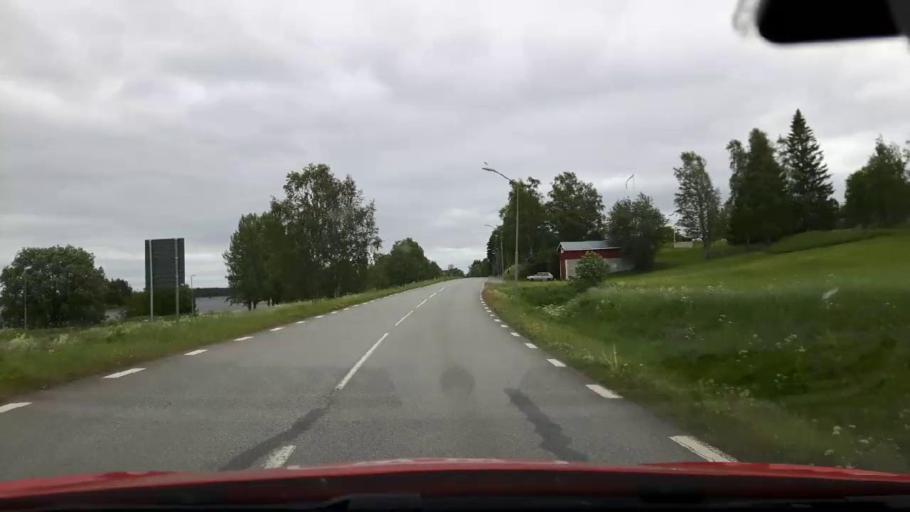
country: SE
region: Jaemtland
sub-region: Stroemsunds Kommun
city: Stroemsund
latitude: 63.5798
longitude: 15.3641
